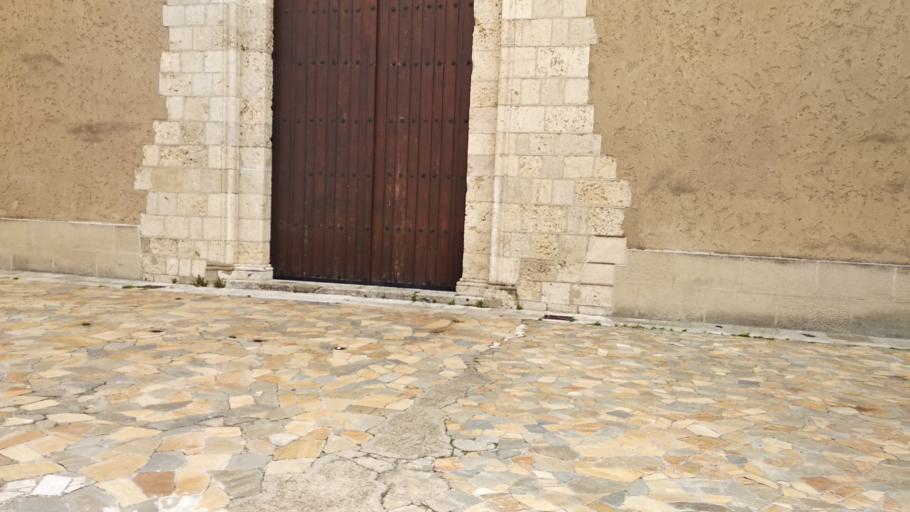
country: IT
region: Sicily
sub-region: Messina
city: Messina
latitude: 38.1983
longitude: 15.5533
